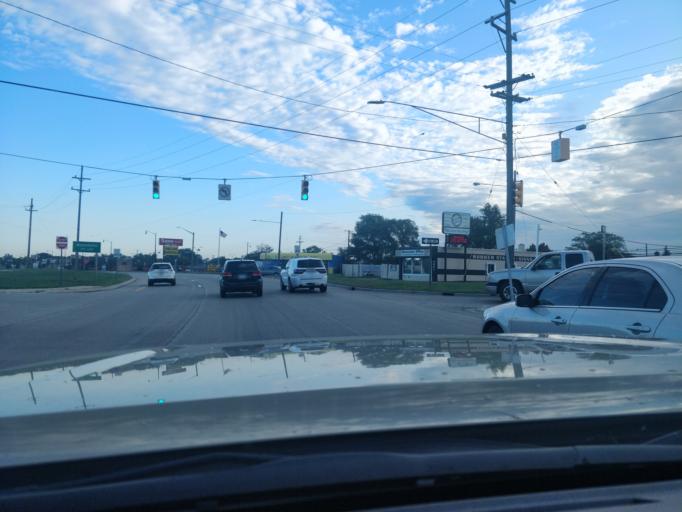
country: US
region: Michigan
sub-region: Wayne County
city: Riverview
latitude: 42.1910
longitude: -83.1802
